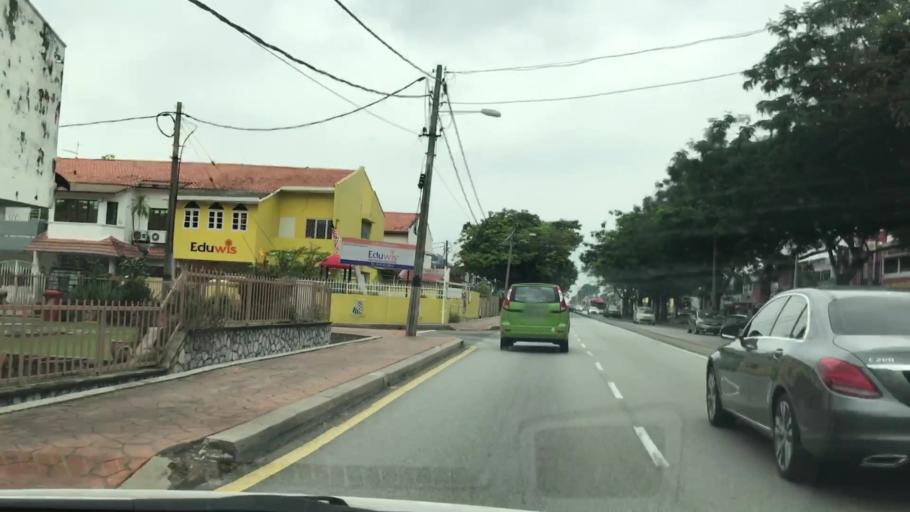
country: MY
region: Selangor
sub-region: Petaling
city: Petaling Jaya
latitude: 3.1154
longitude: 101.6220
